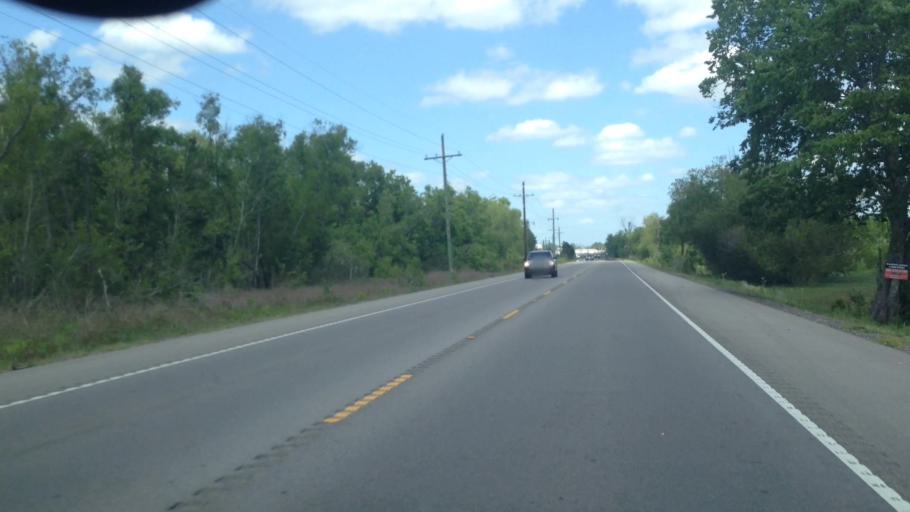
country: US
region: Louisiana
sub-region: Terrebonne Parish
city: Houma
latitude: 29.6385
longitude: -90.6953
